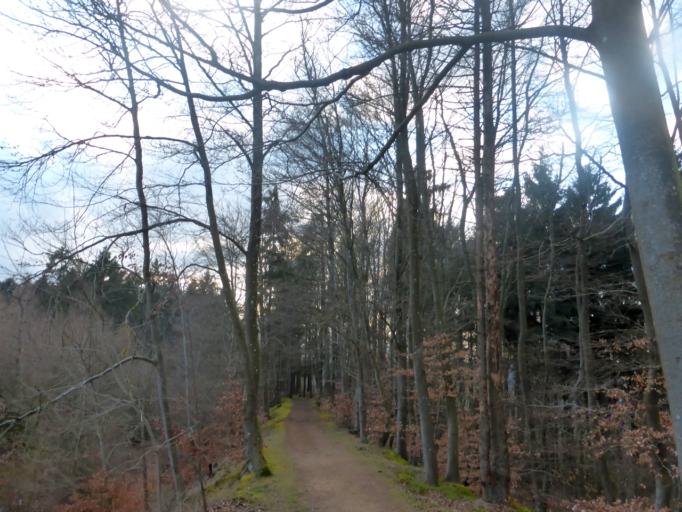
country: LU
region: Luxembourg
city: Belvaux
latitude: 49.5127
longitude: 5.9185
